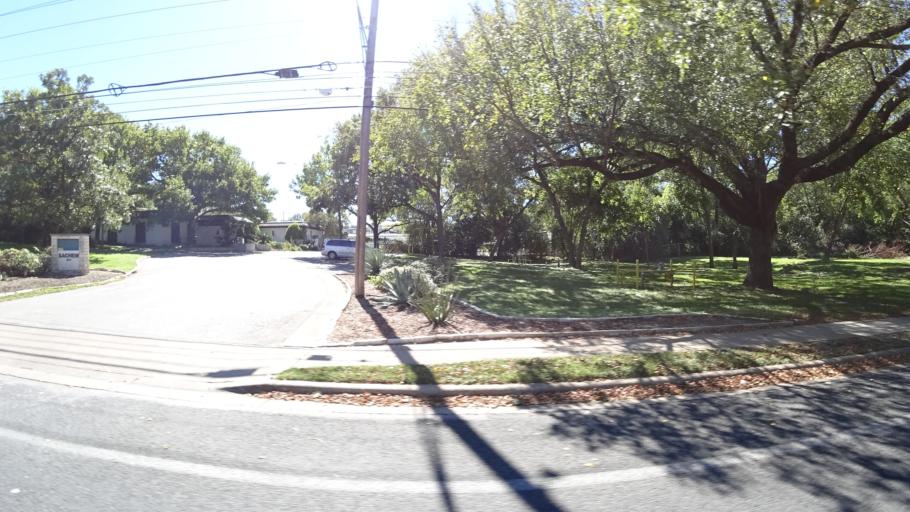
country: US
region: Texas
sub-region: Travis County
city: Austin
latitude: 30.2251
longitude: -97.7507
